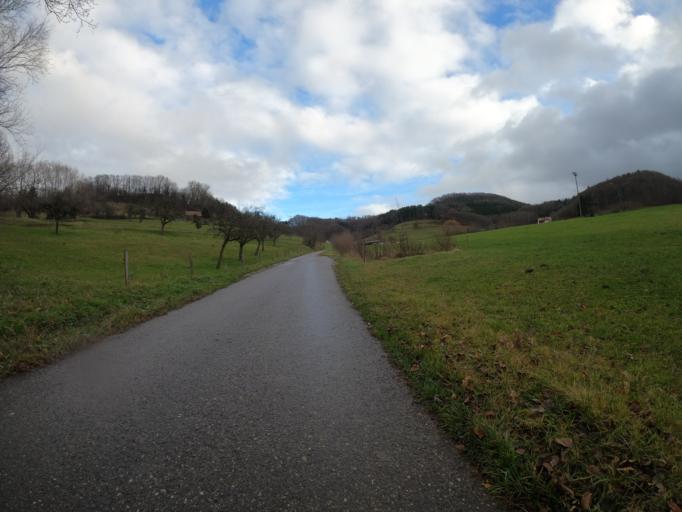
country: DE
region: Baden-Wuerttemberg
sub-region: Regierungsbezirk Stuttgart
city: Waldstetten
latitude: 48.7546
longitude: 9.8359
